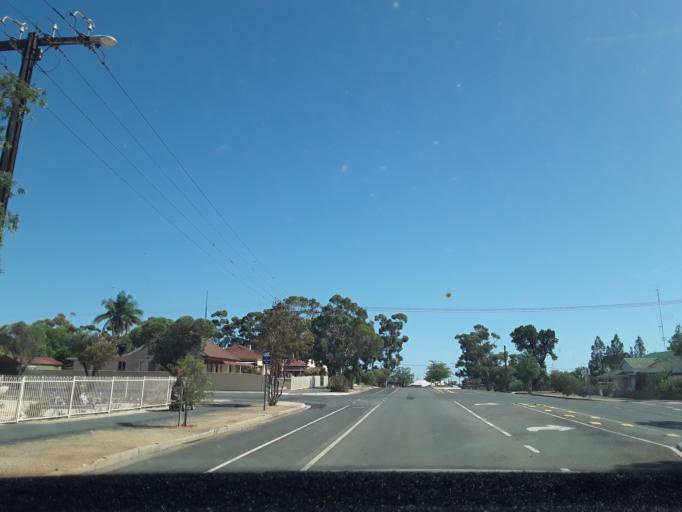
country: AU
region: South Australia
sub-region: Berri and Barmera
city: Barmera
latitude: -34.2544
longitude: 140.4655
